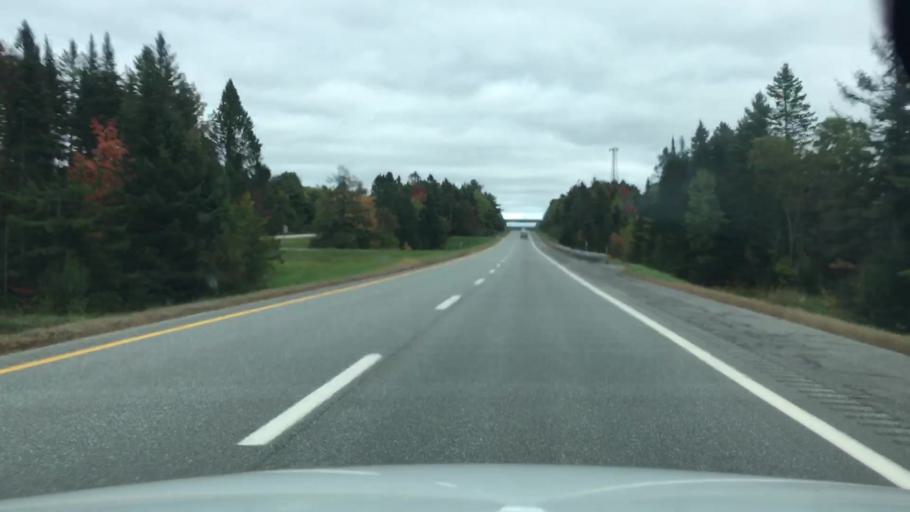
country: US
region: Maine
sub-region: Penobscot County
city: Plymouth
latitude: 44.7883
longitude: -69.1721
